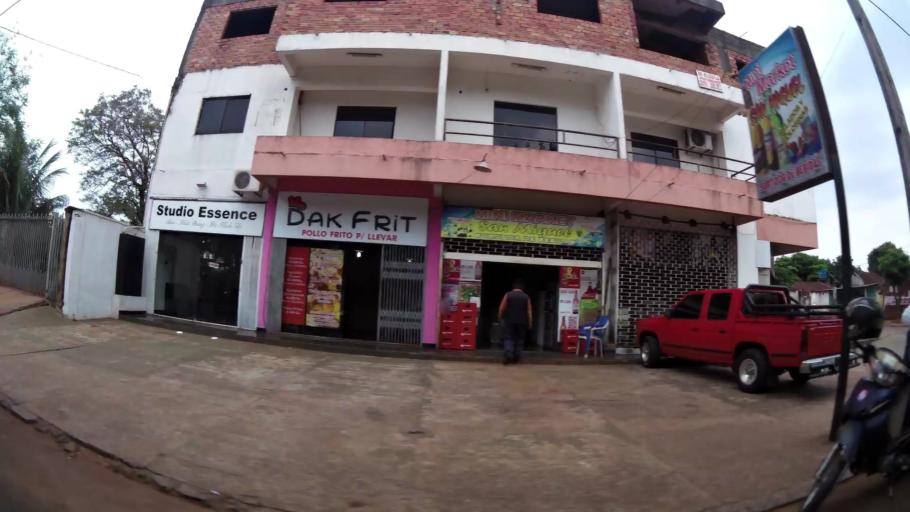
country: PY
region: Alto Parana
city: Presidente Franco
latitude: -25.5197
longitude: -54.6442
